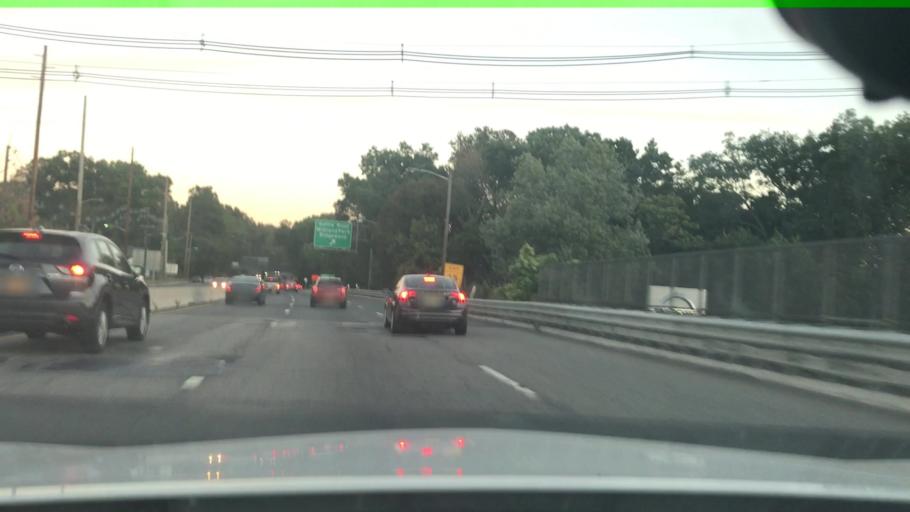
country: US
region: New Jersey
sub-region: Passaic County
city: Hawthorne
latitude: 40.9677
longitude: -74.1546
